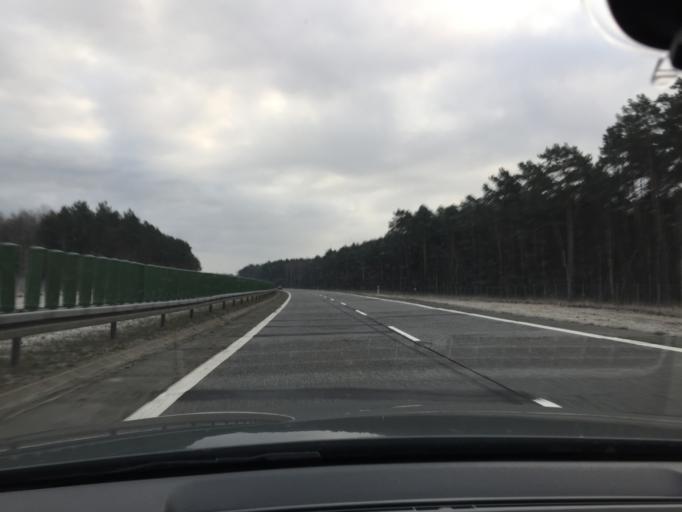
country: PL
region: Lubusz
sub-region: Powiat zarski
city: Trzebiel
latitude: 51.6255
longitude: 14.8860
